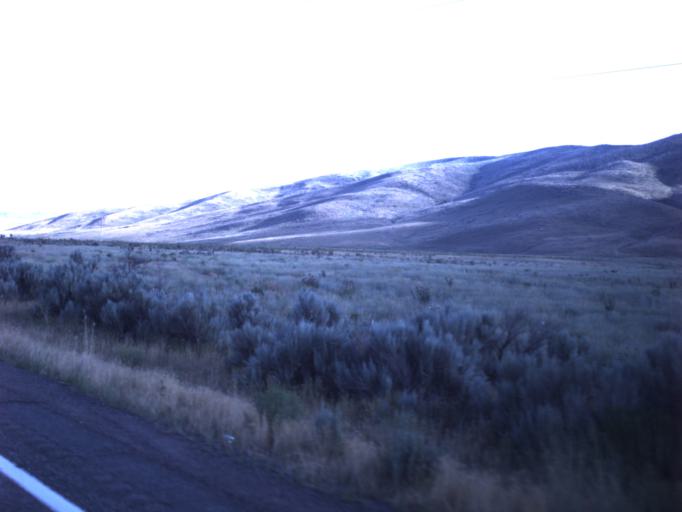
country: US
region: Utah
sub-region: Utah County
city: Woodland Hills
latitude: 39.8481
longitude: -111.5176
